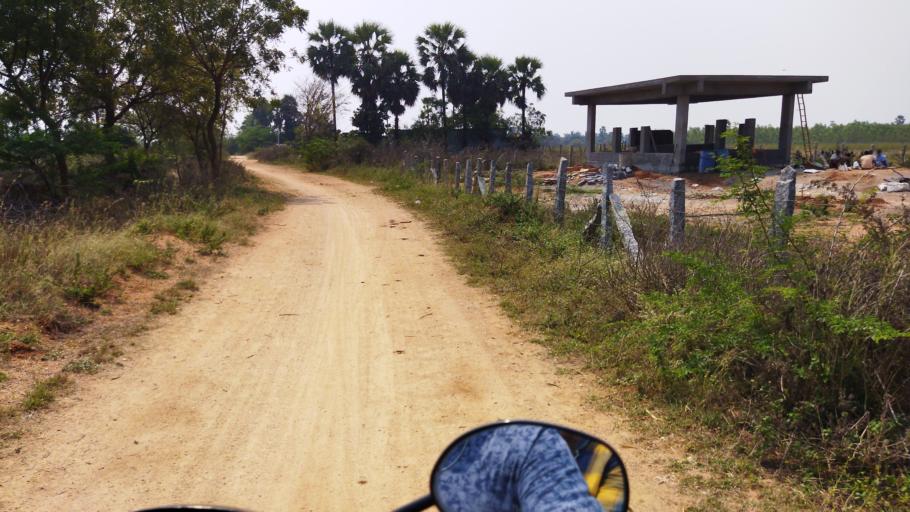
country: IN
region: Telangana
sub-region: Nalgonda
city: Nalgonda
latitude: 17.1525
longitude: 79.4097
